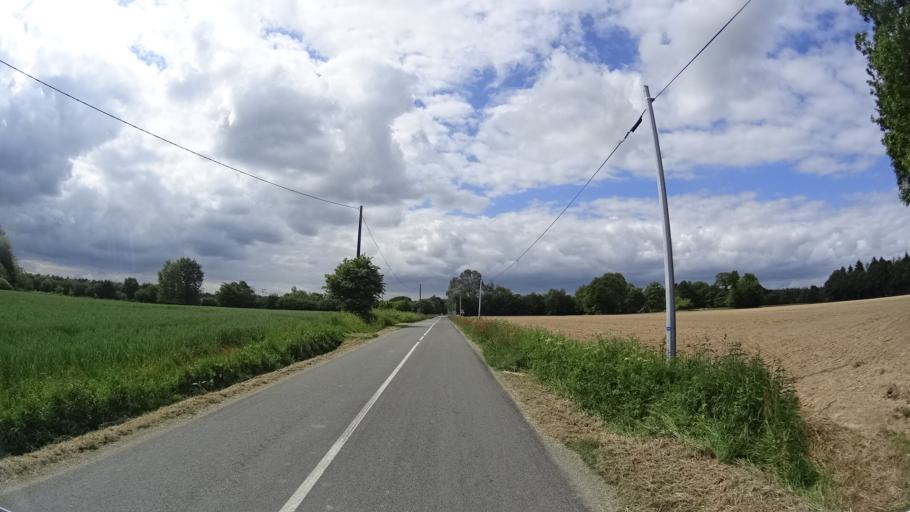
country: FR
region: Brittany
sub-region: Departement d'Ille-et-Vilaine
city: Plelan-le-Grand
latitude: 48.0436
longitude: -2.1001
